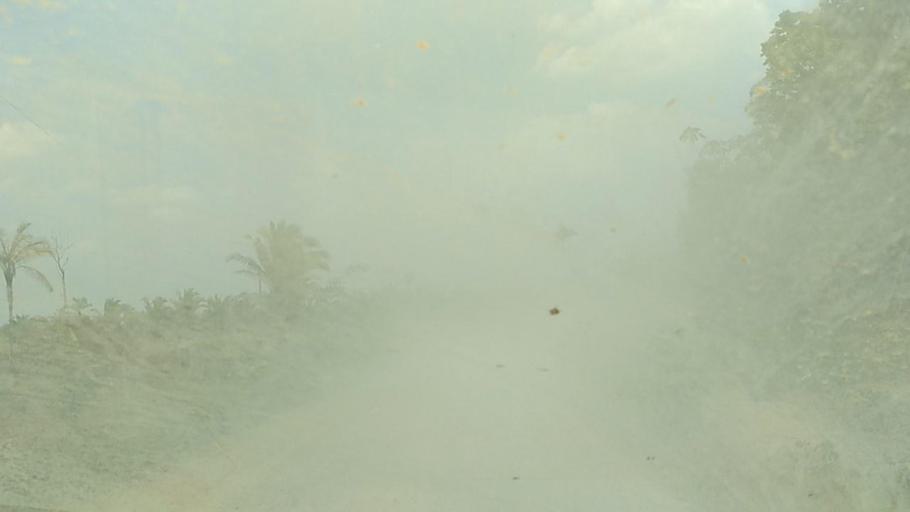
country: BR
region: Rondonia
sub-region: Porto Velho
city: Porto Velho
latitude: -8.7285
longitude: -63.3102
